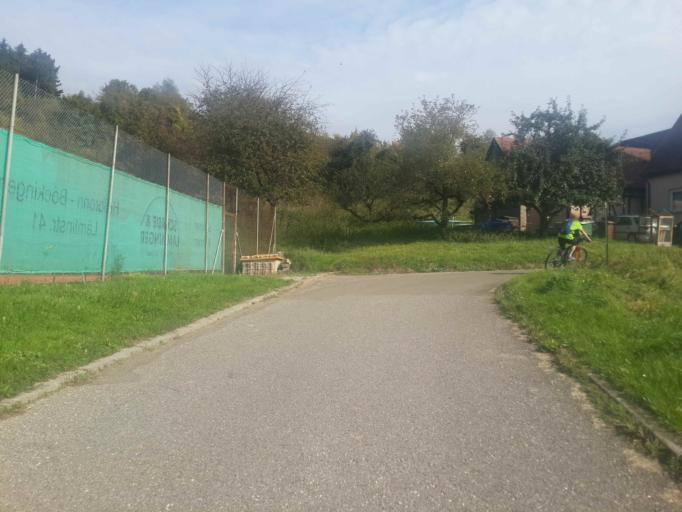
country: DE
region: Baden-Wuerttemberg
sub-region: Regierungsbezirk Stuttgart
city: Neudenau
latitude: 49.2896
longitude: 9.2841
